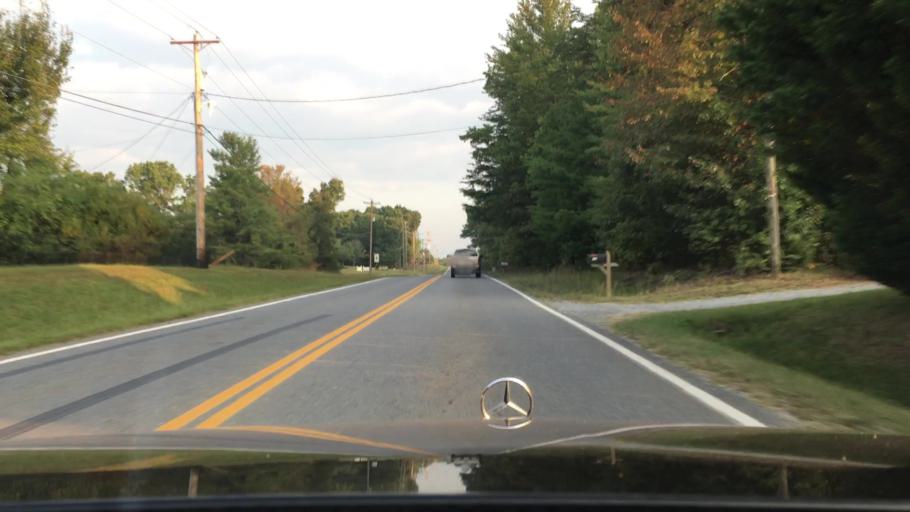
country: US
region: Virginia
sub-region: Campbell County
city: Timberlake
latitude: 37.3055
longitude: -79.2155
